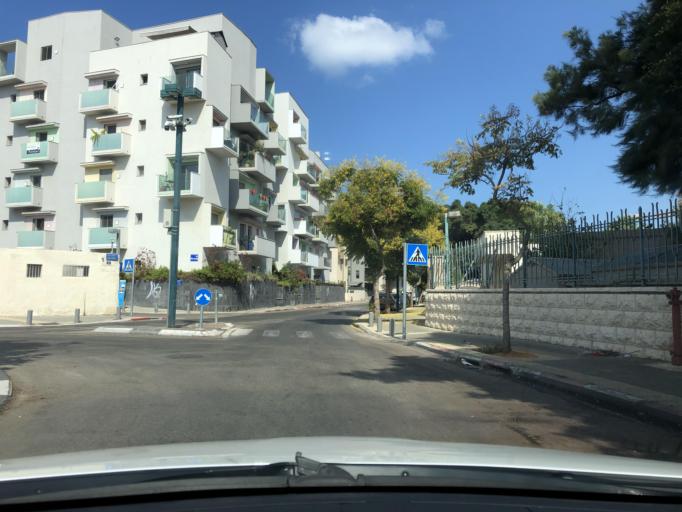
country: IL
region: Tel Aviv
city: Yafo
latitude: 32.0441
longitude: 34.7567
